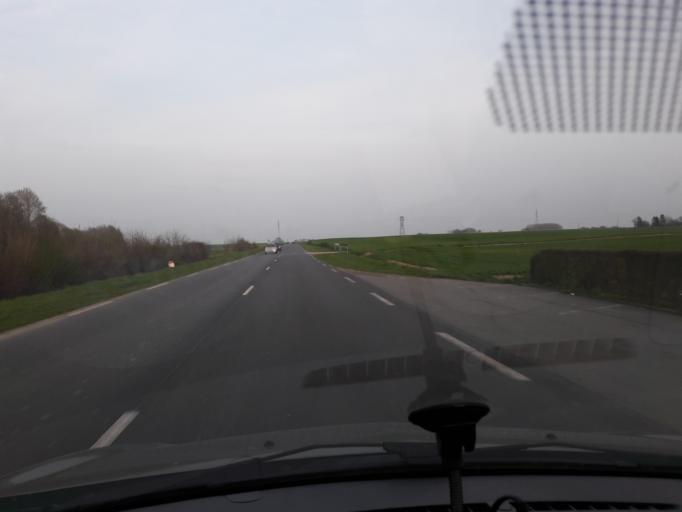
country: FR
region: Nord-Pas-de-Calais
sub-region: Departement du Nord
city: Recquignies
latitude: 50.2589
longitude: 4.0350
